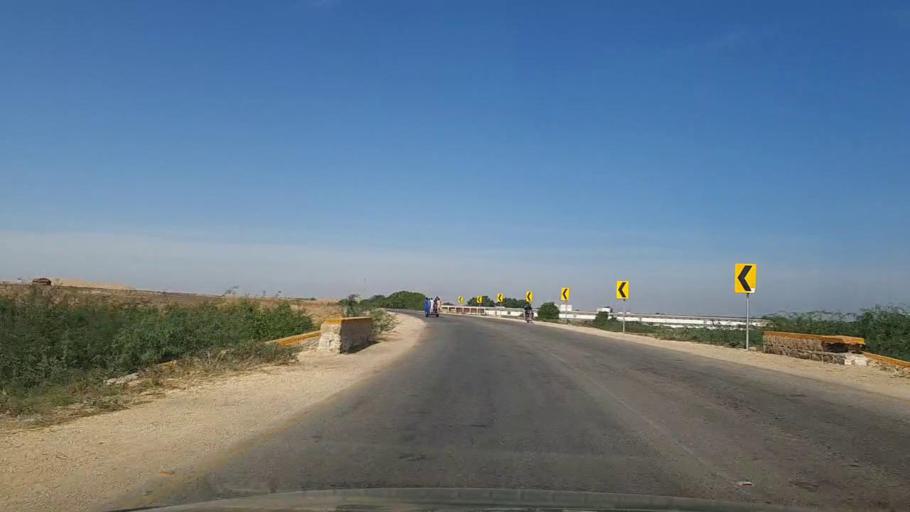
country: PK
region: Sindh
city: Kotri
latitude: 25.1874
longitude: 68.2400
